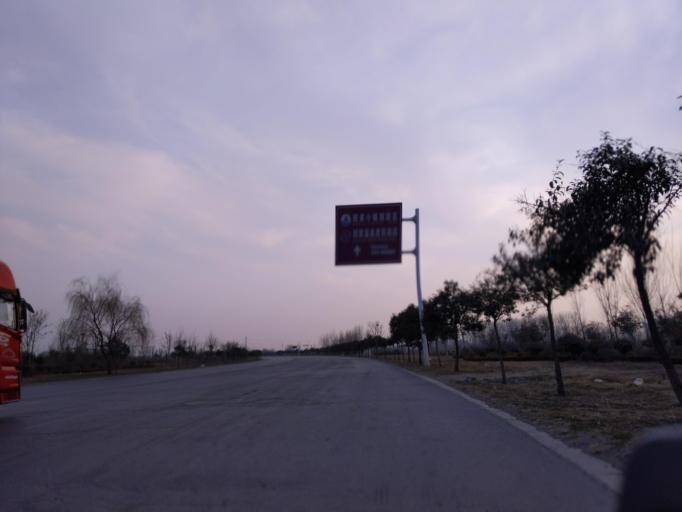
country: CN
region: Henan Sheng
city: Puyang
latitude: 35.8151
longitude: 114.9678
